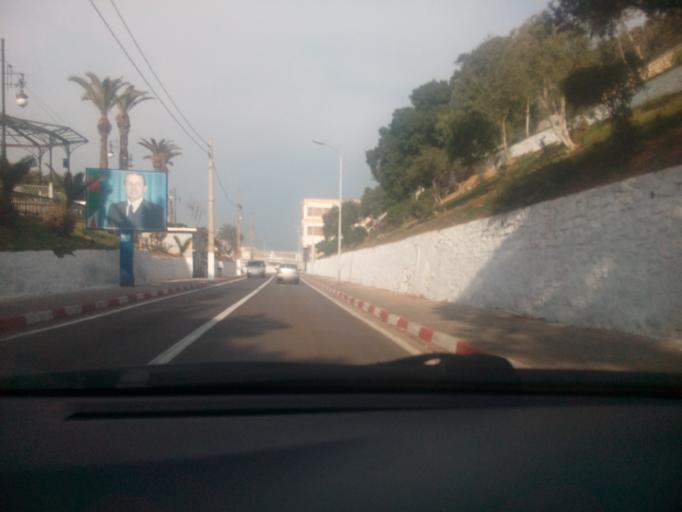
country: DZ
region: Oran
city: Oran
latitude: 35.7059
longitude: -0.6518
